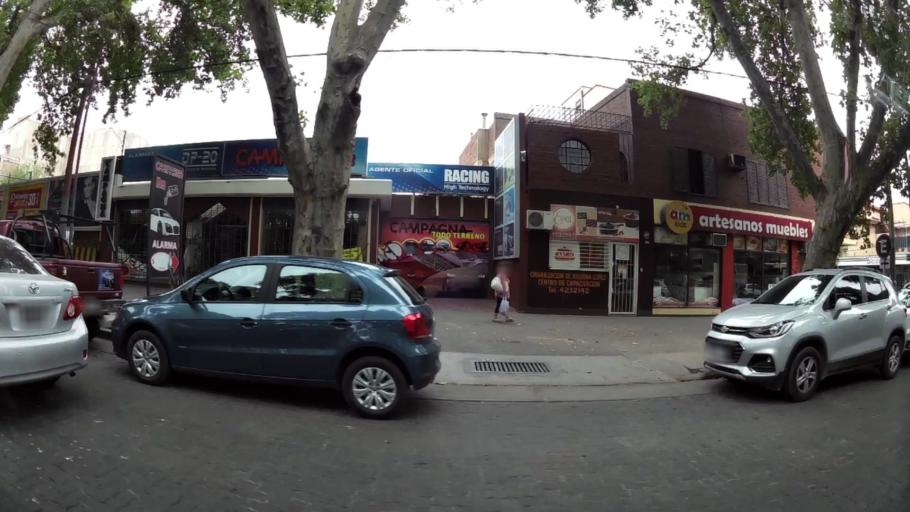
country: AR
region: Mendoza
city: Mendoza
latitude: -32.8778
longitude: -68.8361
